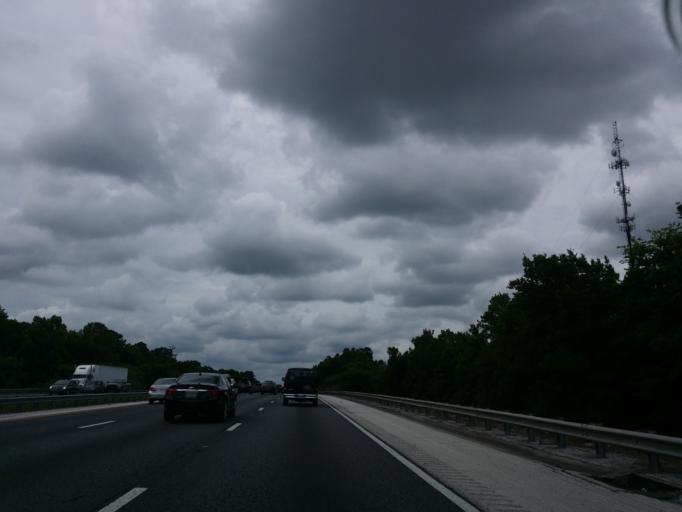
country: US
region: Florida
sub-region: Marion County
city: Citra
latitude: 29.3458
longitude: -82.2185
